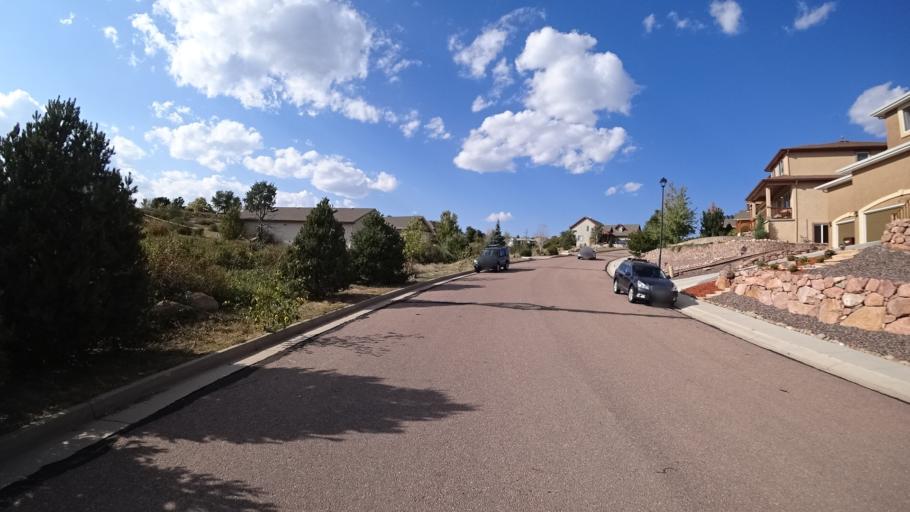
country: US
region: Colorado
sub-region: El Paso County
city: Cimarron Hills
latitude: 38.9087
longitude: -104.7382
